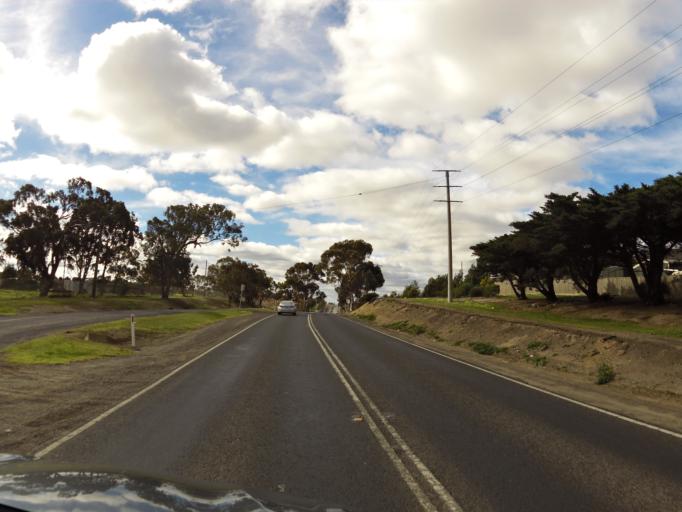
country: AU
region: Victoria
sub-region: Hume
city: Meadow Heights
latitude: -37.6378
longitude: 144.9059
